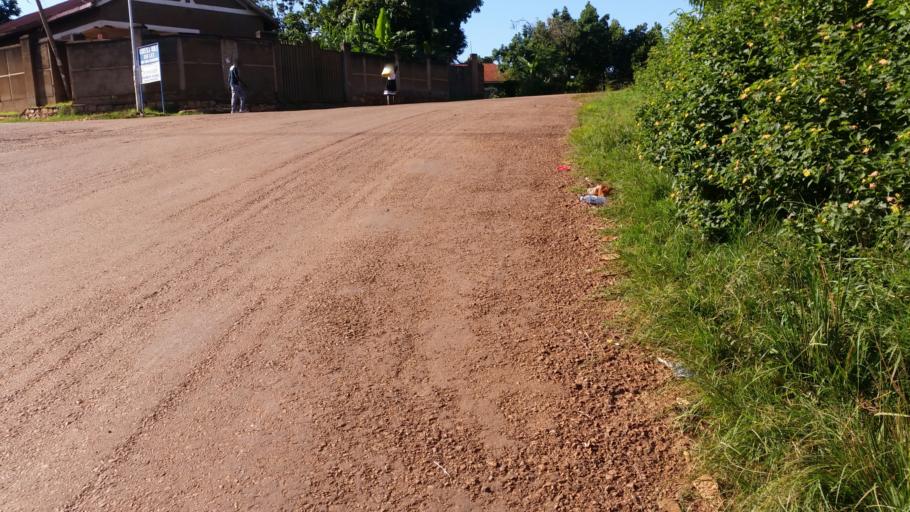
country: UG
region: Central Region
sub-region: Wakiso District
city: Kireka
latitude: 0.3378
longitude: 32.6467
